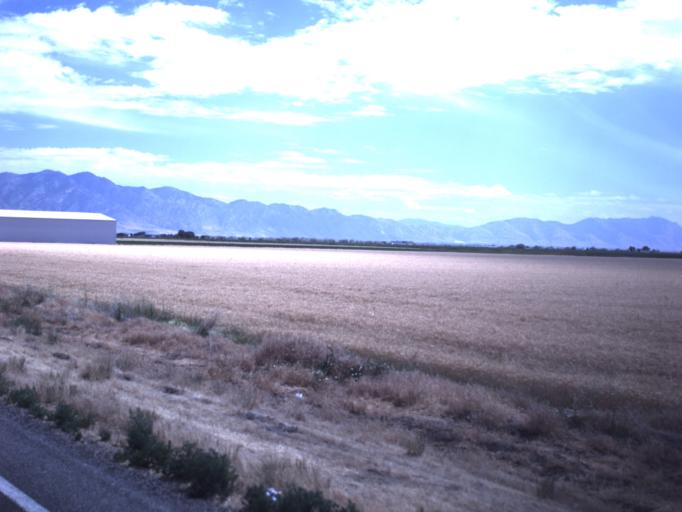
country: US
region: Utah
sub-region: Box Elder County
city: Tremonton
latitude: 41.7094
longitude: -112.2773
